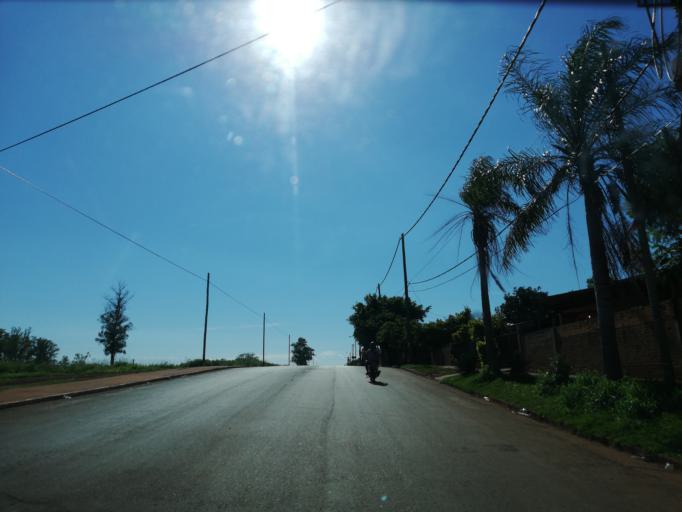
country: AR
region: Misiones
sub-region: Departamento de Capital
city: Posadas
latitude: -27.4329
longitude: -55.9414
